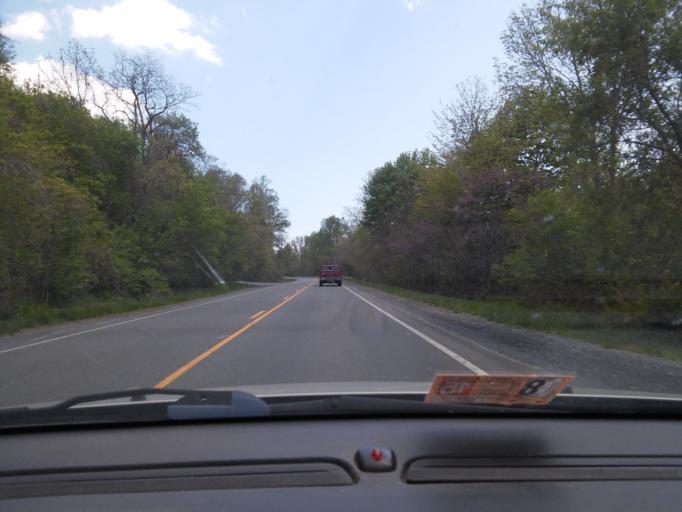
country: US
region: Virginia
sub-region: Warren County
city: Apple Mountain Lake
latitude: 38.8734
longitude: -78.1438
